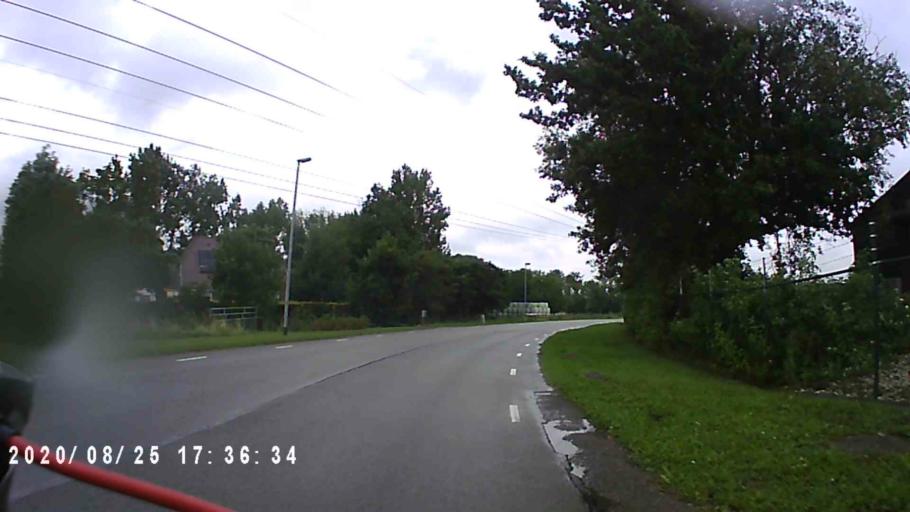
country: NL
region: Groningen
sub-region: Gemeente Zuidhorn
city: Aduard
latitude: 53.2204
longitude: 6.4836
